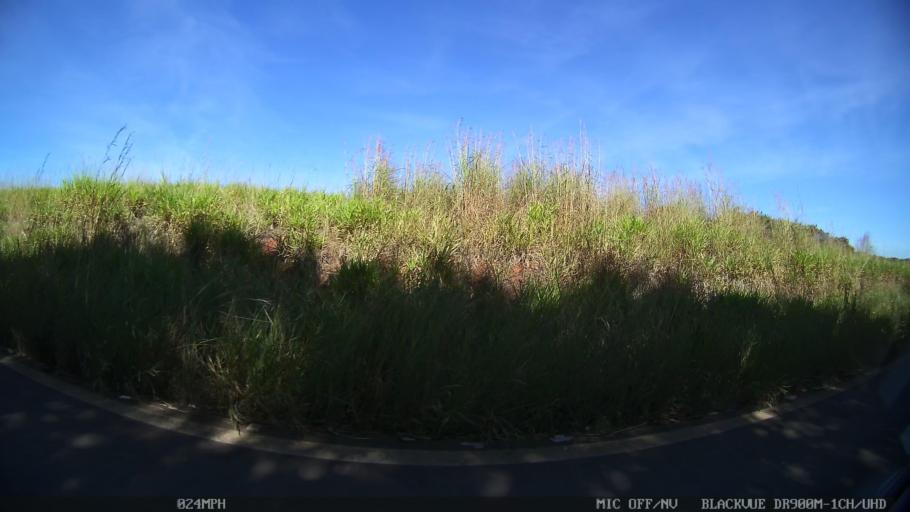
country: BR
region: Sao Paulo
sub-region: Franca
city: Franca
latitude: -20.5464
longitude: -47.4665
